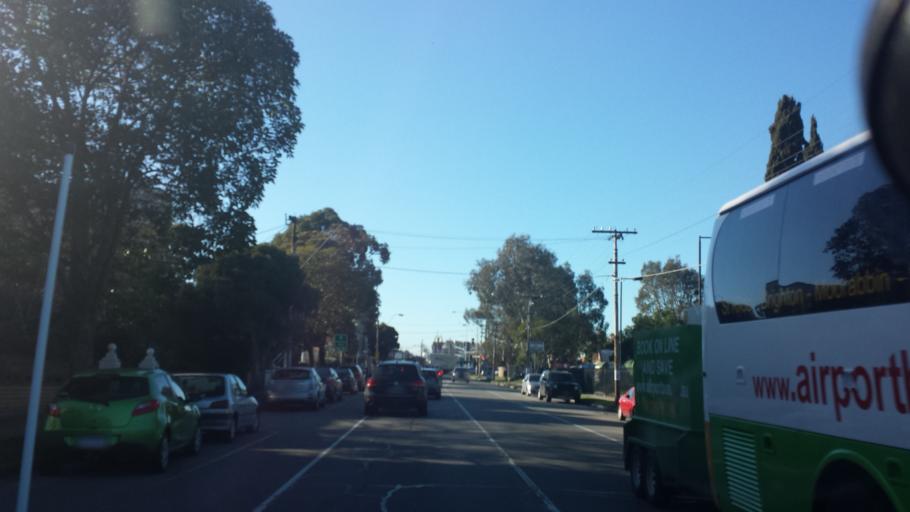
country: AU
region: Victoria
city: Ripponlea
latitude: -37.8837
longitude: 144.9950
